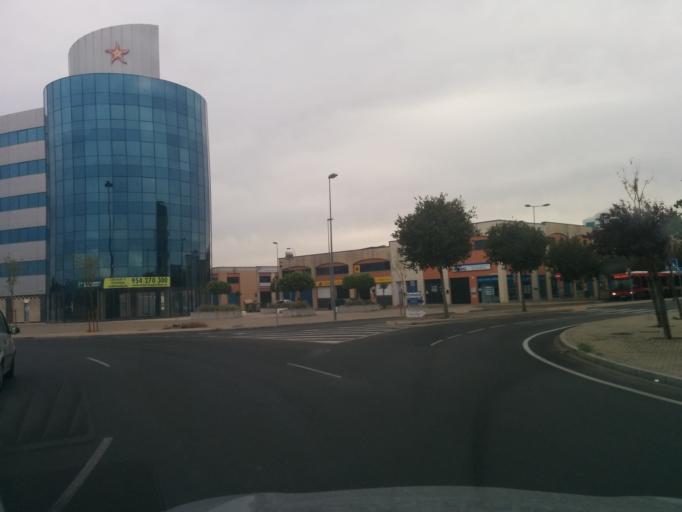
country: ES
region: Andalusia
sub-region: Provincia de Sevilla
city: Sevilla
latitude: 37.4272
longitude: -5.9782
